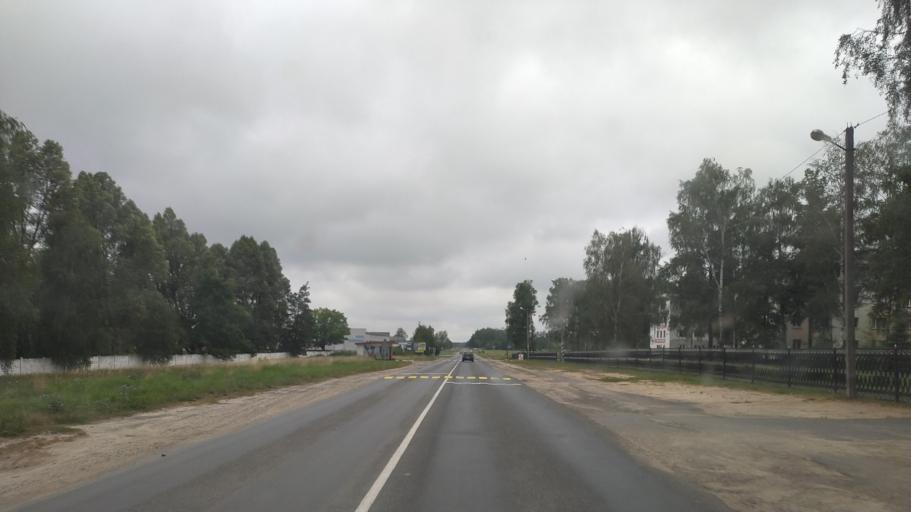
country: BY
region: Brest
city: Byaroza
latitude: 52.5510
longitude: 24.9382
